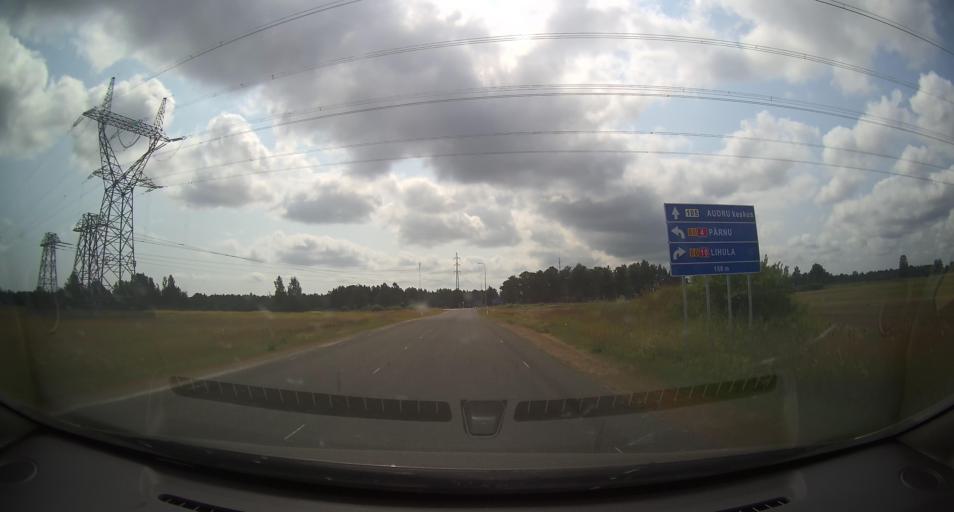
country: EE
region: Paernumaa
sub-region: Audru vald
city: Audru
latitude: 58.4258
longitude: 24.3153
